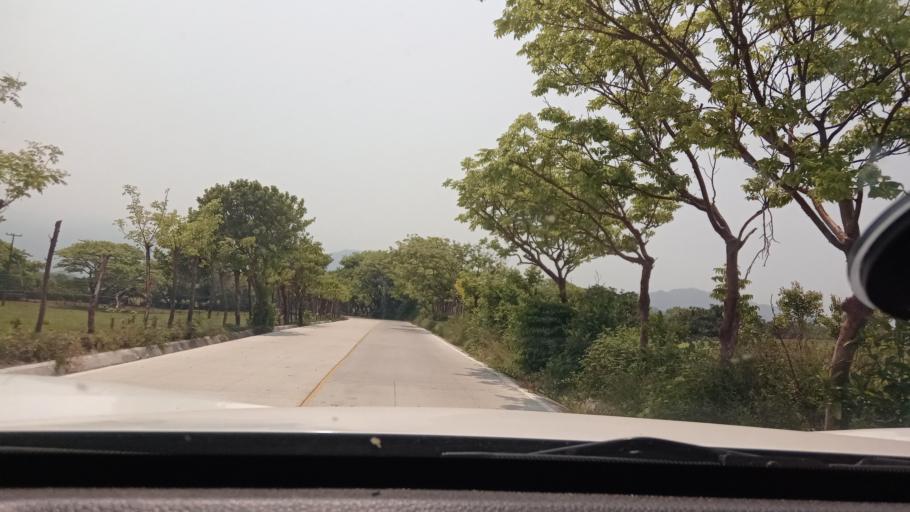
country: MX
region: Veracruz
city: Catemaco
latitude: 18.5602
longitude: -95.0243
